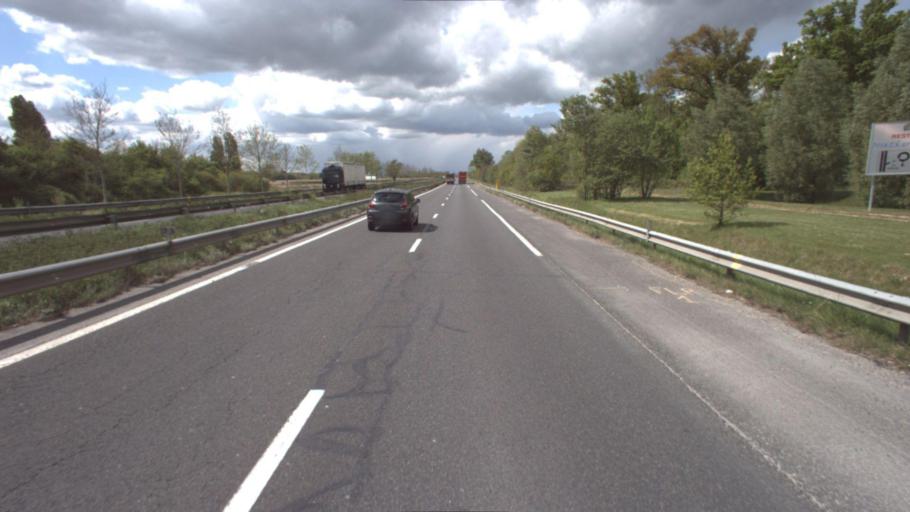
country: FR
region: Ile-de-France
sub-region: Departement de Seine-et-Marne
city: Fontenay-Tresigny
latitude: 48.7231
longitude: 2.8326
